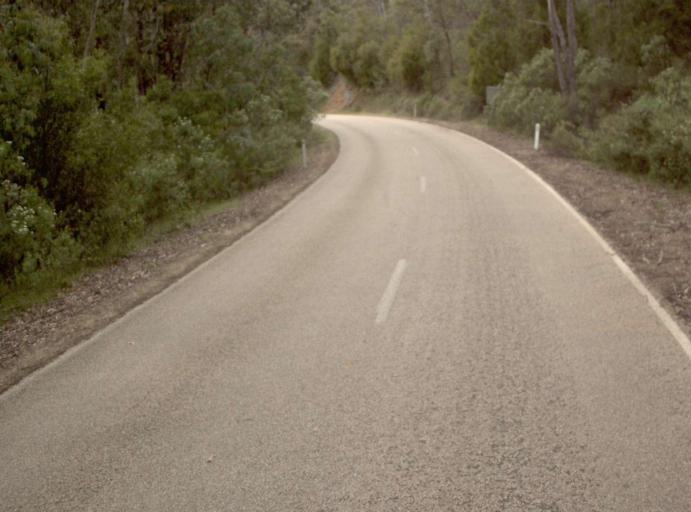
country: AU
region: Victoria
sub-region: East Gippsland
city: Bairnsdale
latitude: -37.6263
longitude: 147.1966
